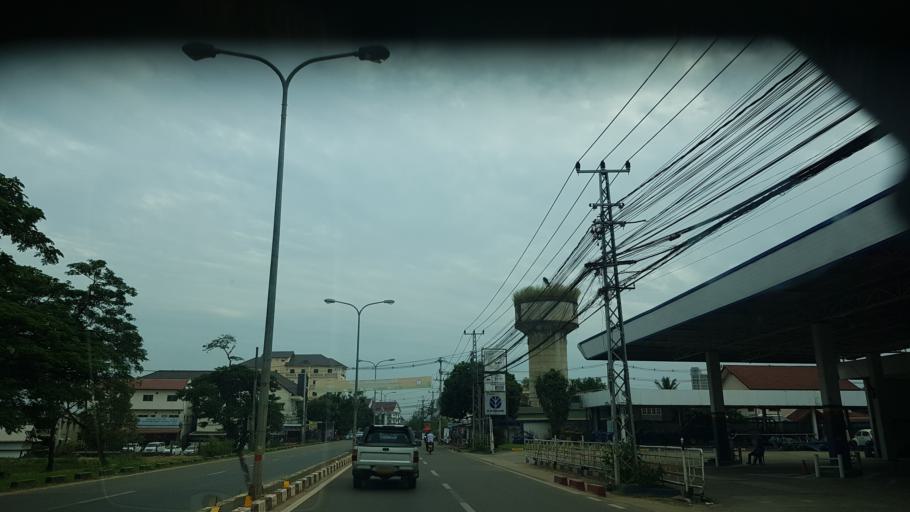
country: LA
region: Vientiane
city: Vientiane
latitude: 17.9507
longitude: 102.6192
